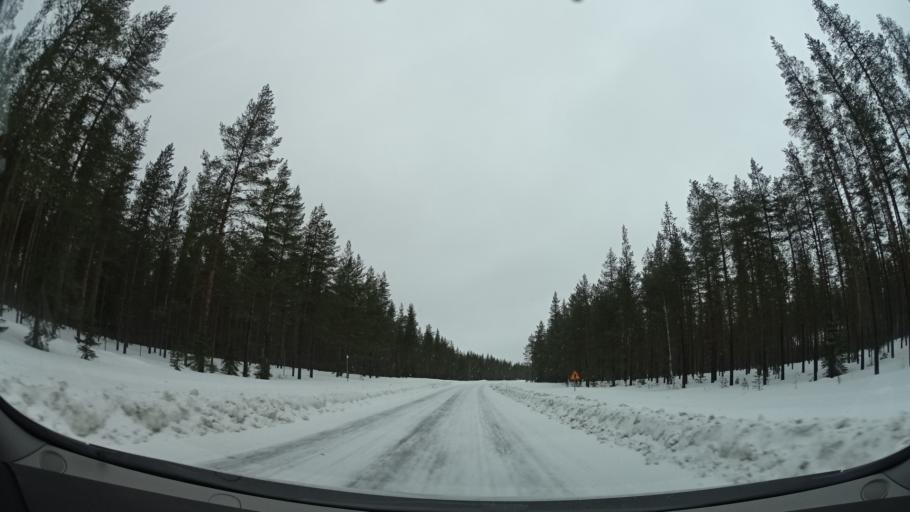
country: SE
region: Vaesterbotten
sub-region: Mala Kommun
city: Mala
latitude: 65.1224
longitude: 18.8750
